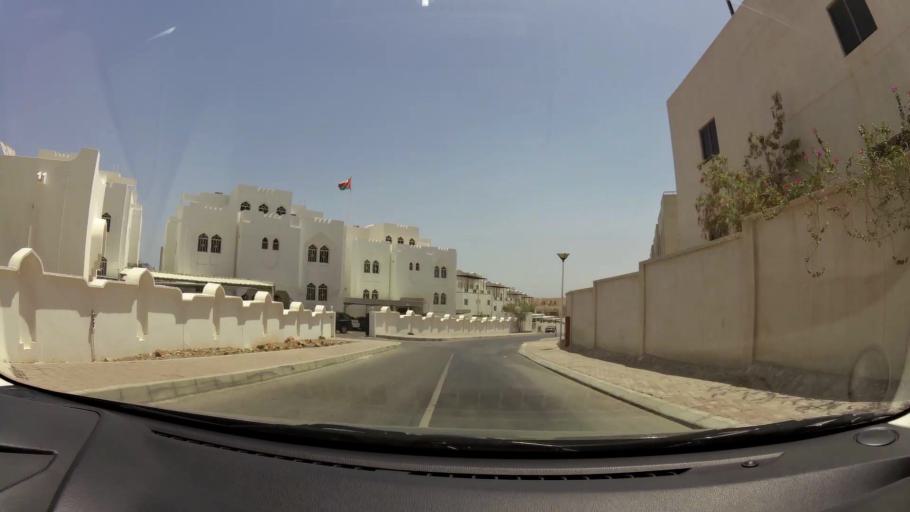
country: OM
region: Muhafazat Masqat
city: Bawshar
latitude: 23.5996
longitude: 58.4717
